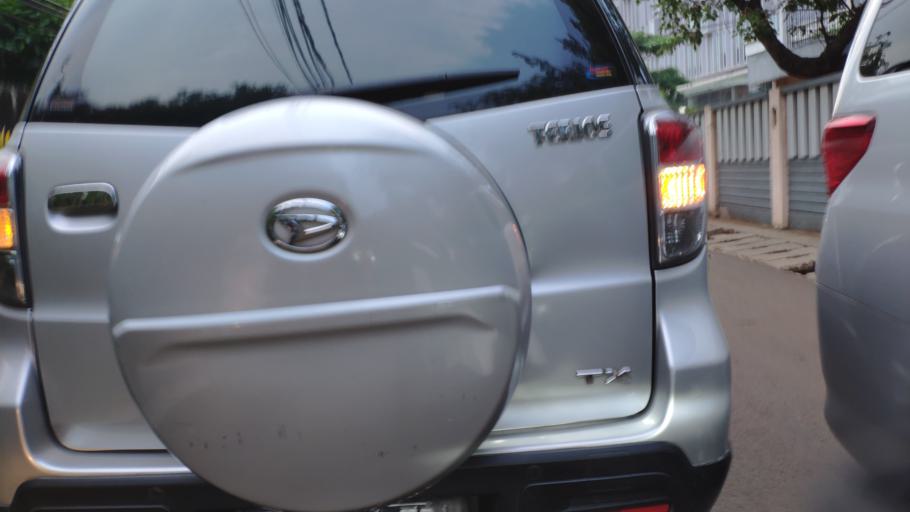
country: ID
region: West Java
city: Pamulang
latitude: -6.2941
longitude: 106.8029
